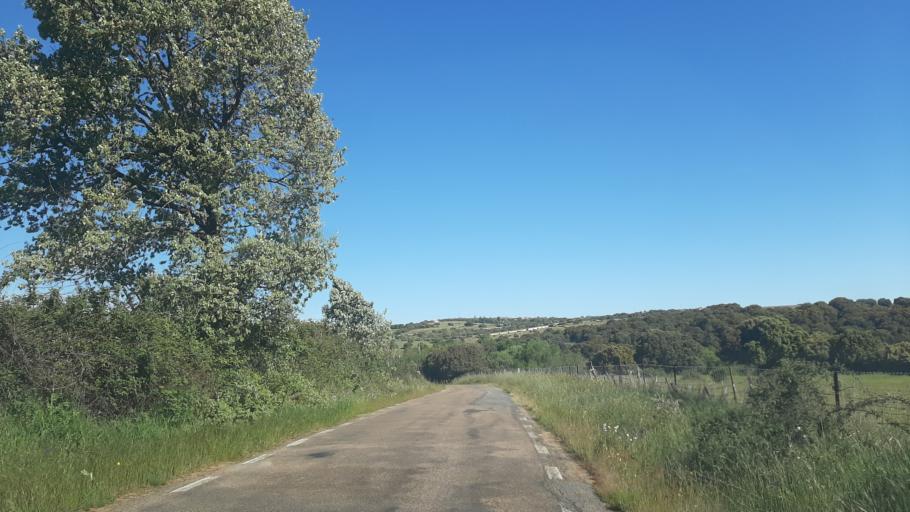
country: ES
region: Castille and Leon
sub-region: Provincia de Salamanca
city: Guijo de Avila
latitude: 40.5332
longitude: -5.6473
